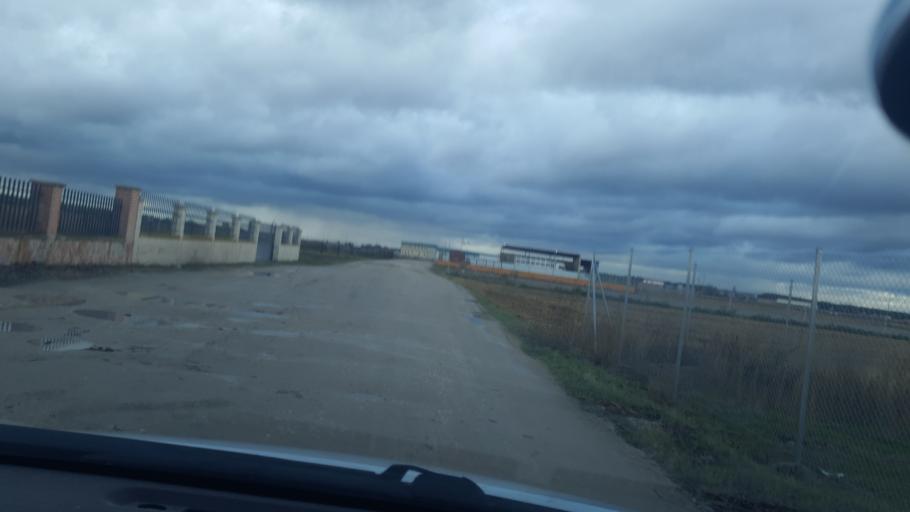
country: ES
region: Castille and Leon
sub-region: Provincia de Segovia
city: Sanchonuno
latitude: 41.2915
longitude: -4.3295
